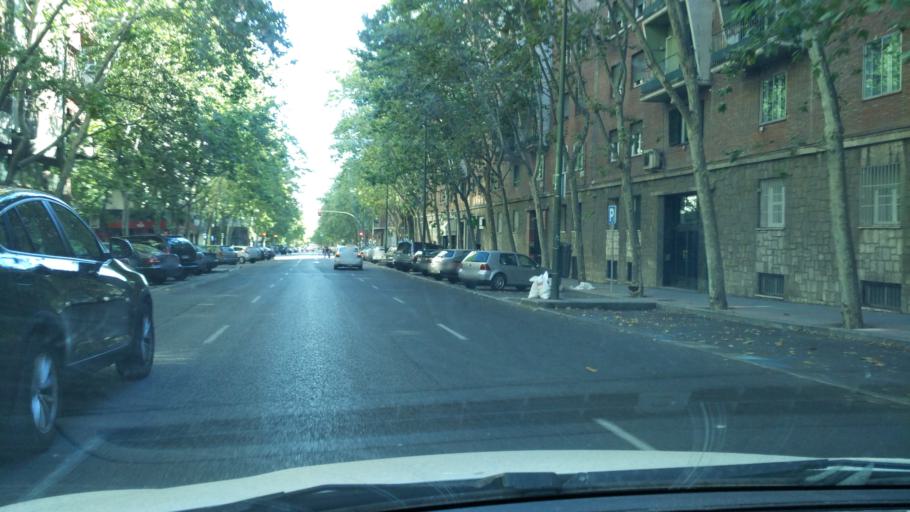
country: ES
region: Madrid
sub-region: Provincia de Madrid
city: Chamartin
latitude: 40.4575
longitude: -3.6945
